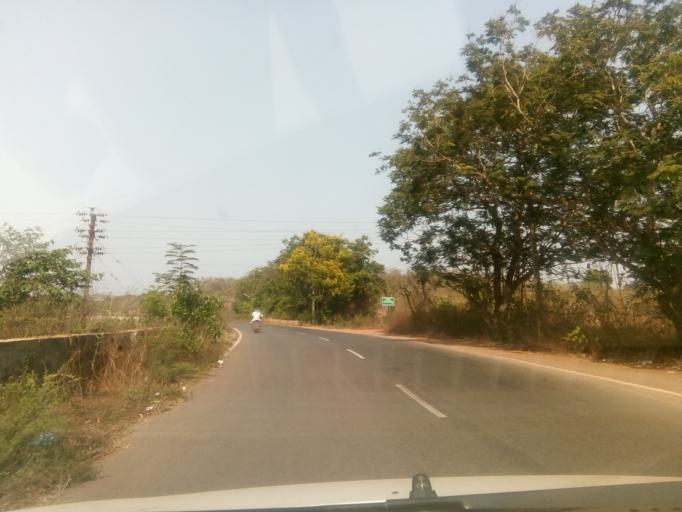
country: IN
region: Goa
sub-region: North Goa
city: Colovale
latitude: 15.6832
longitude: 73.8357
